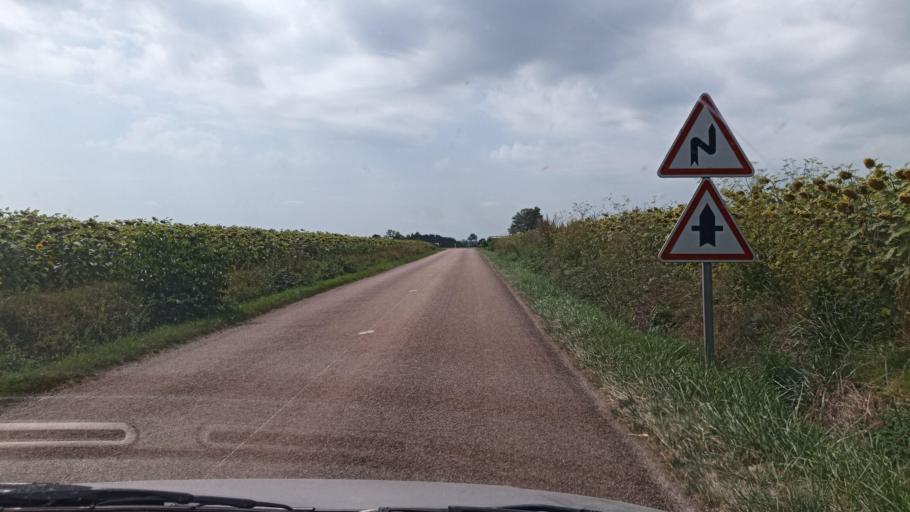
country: FR
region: Bourgogne
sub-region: Departement de l'Yonne
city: Egriselles-le-Bocage
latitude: 48.0401
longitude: 3.2011
